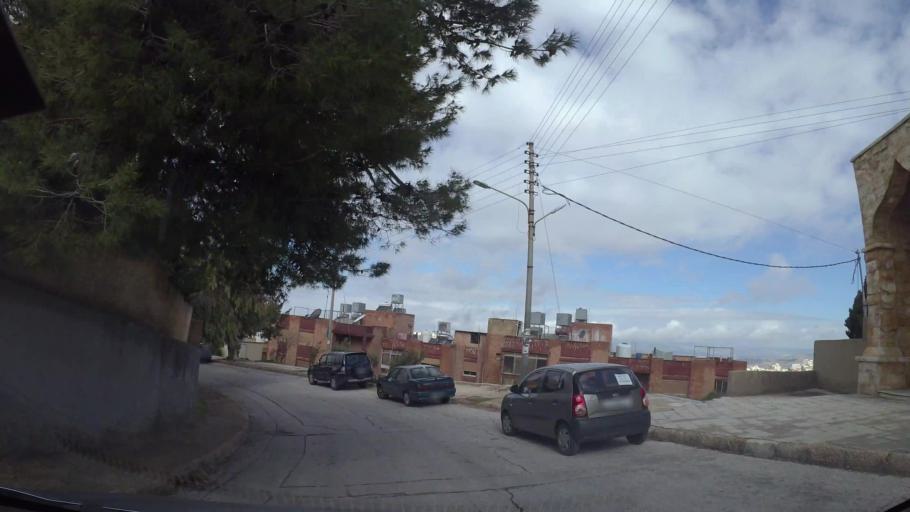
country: JO
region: Amman
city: Al Jubayhah
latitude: 32.0563
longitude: 35.8774
